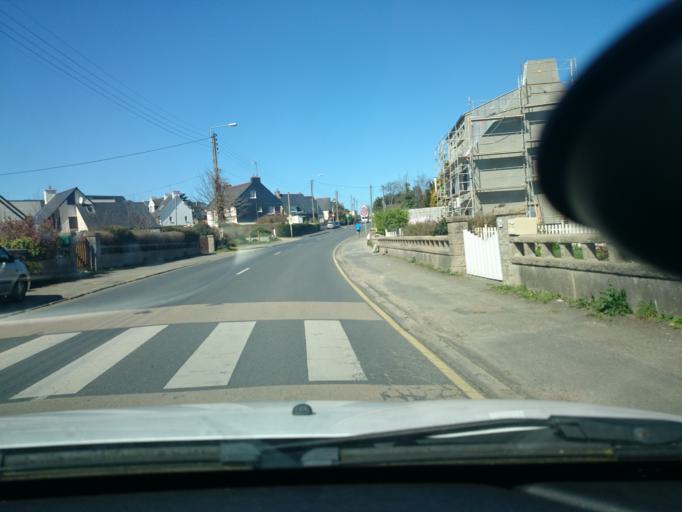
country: FR
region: Brittany
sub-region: Departement des Cotes-d'Armor
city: Tregastel
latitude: 48.8234
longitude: -3.5037
